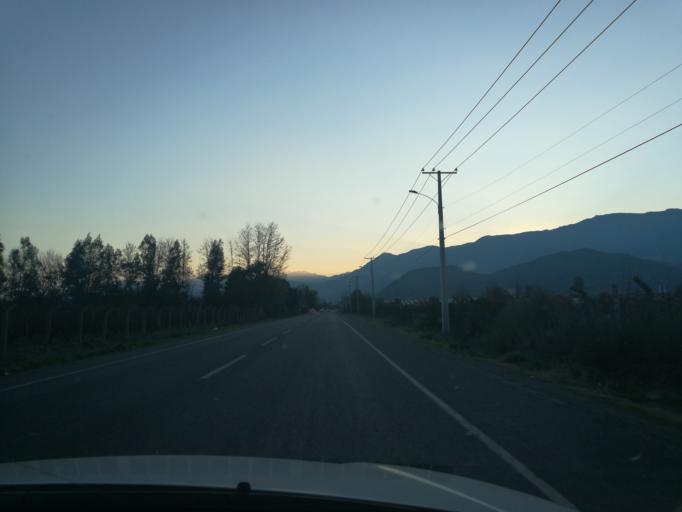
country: CL
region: O'Higgins
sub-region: Provincia de Cachapoal
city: Graneros
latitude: -34.0386
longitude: -70.6921
